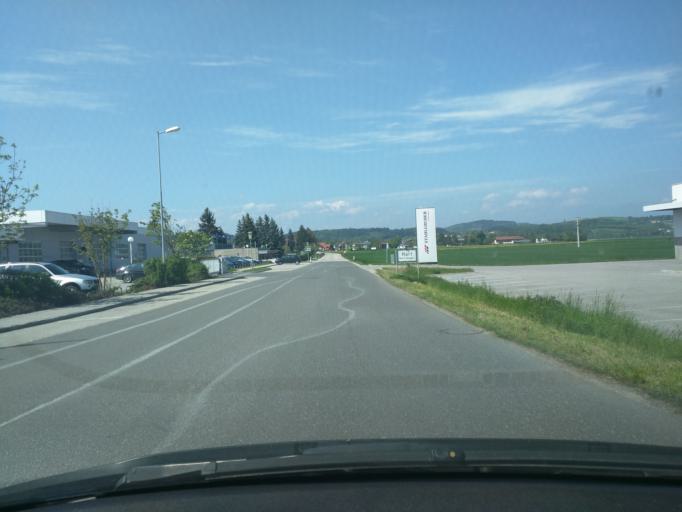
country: AT
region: Lower Austria
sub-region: Politischer Bezirk Amstetten
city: Sankt Georgen am Ybbsfelde
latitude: 48.1135
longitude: 14.9258
